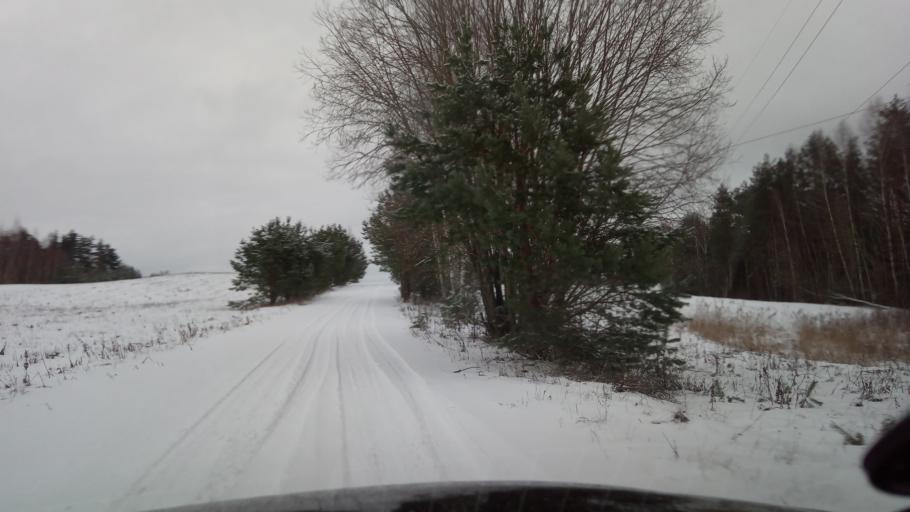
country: LT
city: Zarasai
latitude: 55.6694
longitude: 26.0901
